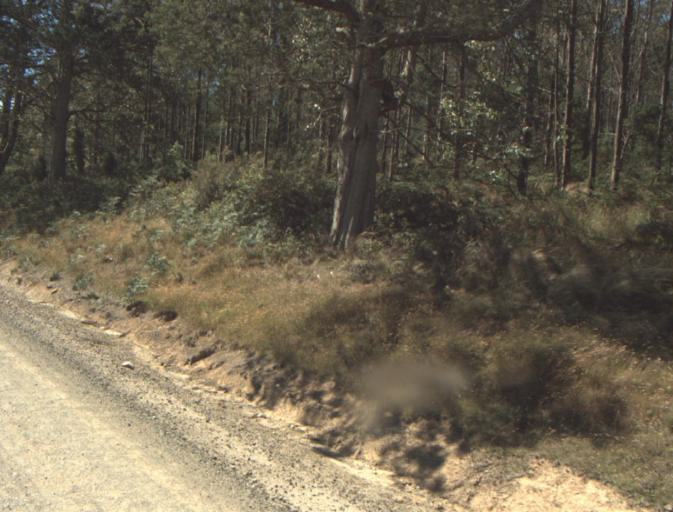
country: AU
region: Tasmania
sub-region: Dorset
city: Scottsdale
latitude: -41.3410
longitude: 147.4310
